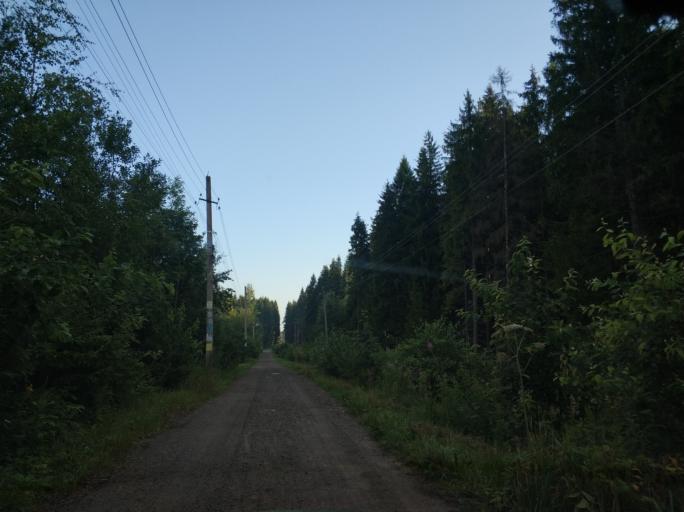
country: RU
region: Leningrad
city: Shcheglovo
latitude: 60.0539
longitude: 30.7511
